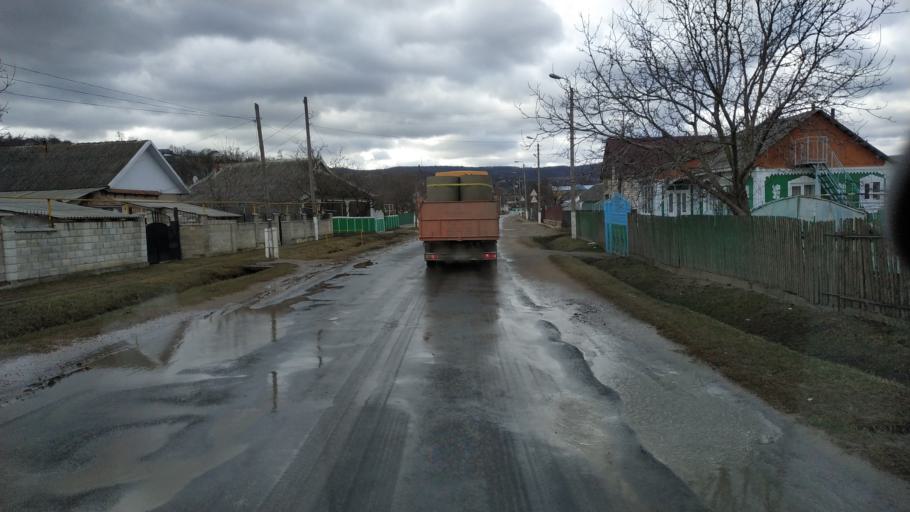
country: MD
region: Stinga Nistrului
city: Bucovat
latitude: 47.1593
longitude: 28.4334
